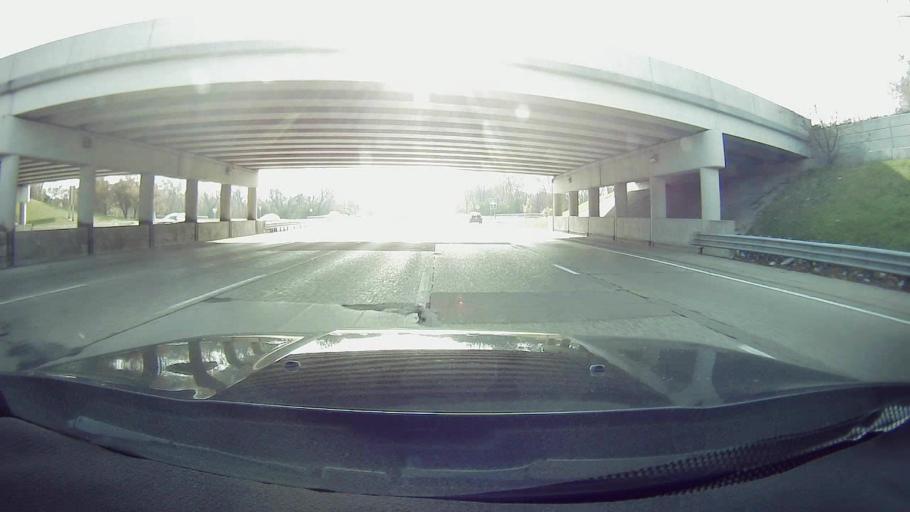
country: US
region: Michigan
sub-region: Wayne County
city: Redford
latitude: 42.4428
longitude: -83.2785
